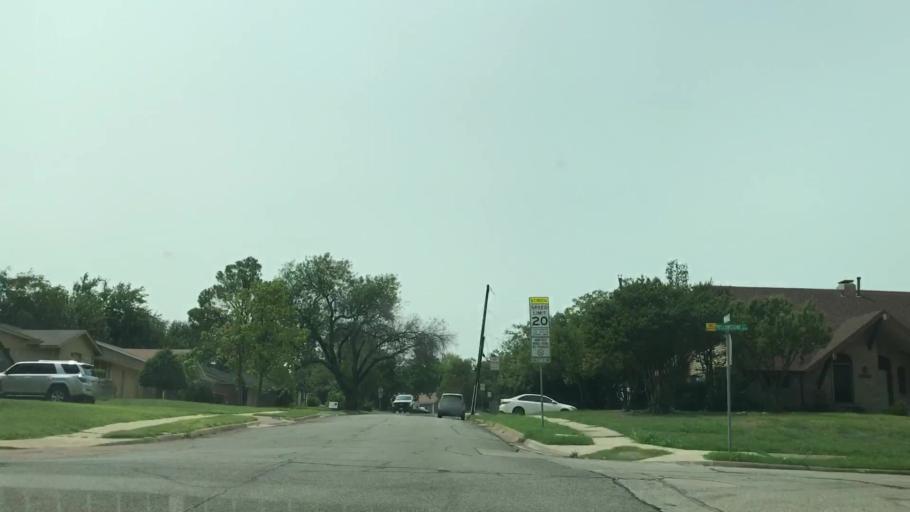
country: US
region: Texas
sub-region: Dallas County
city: Irving
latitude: 32.8419
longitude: -97.0011
